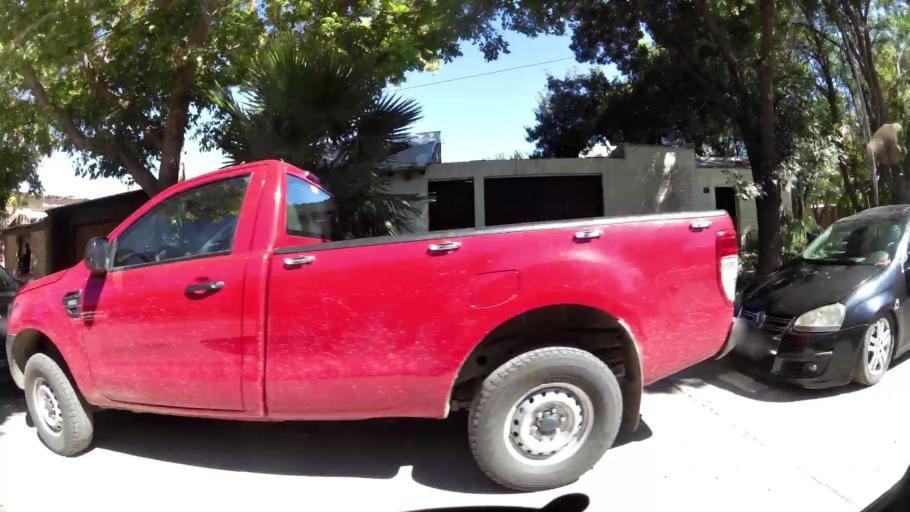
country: AR
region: Mendoza
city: Las Heras
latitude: -32.8329
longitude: -68.8446
